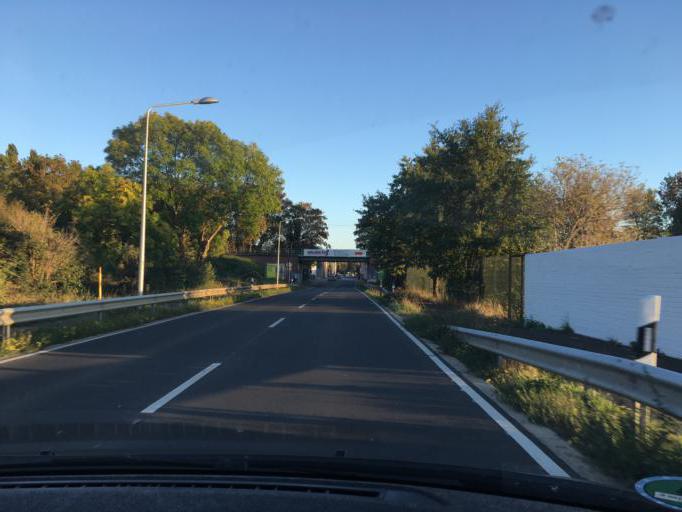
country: DE
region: North Rhine-Westphalia
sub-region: Regierungsbezirk Koln
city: Dueren
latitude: 50.8014
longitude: 6.4647
